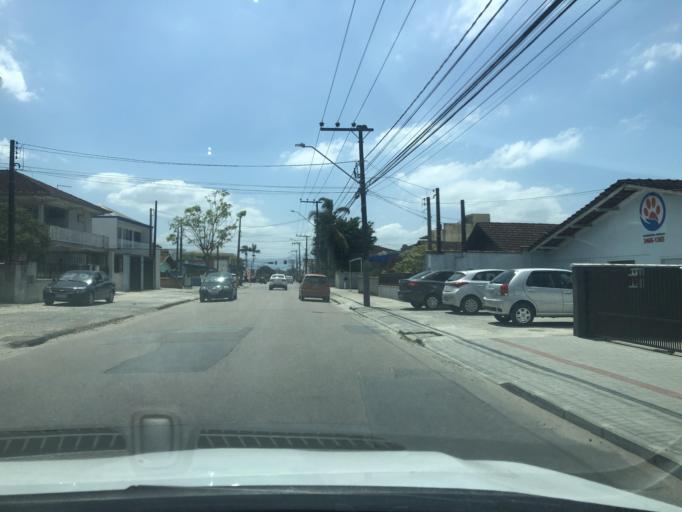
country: BR
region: Santa Catarina
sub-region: Joinville
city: Joinville
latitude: -26.3336
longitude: -48.8154
